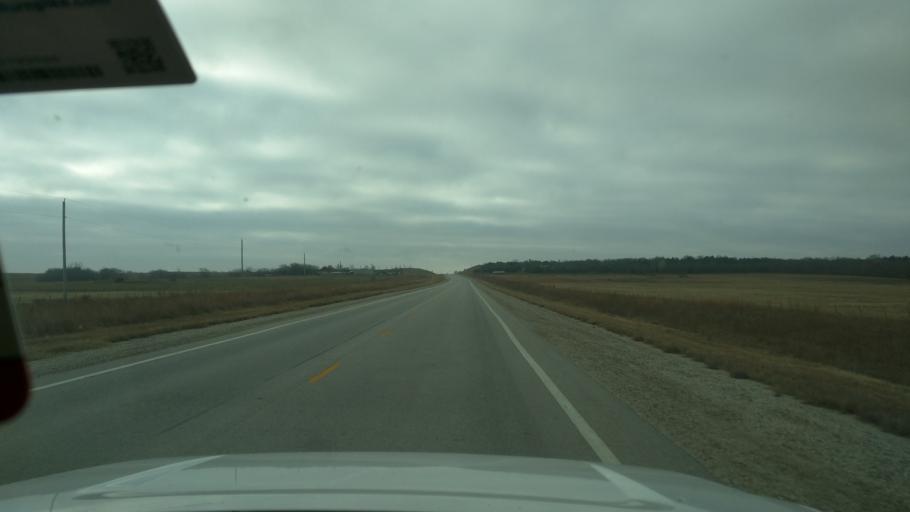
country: US
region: Kansas
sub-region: Elk County
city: Howard
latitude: 37.6133
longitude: -96.2534
